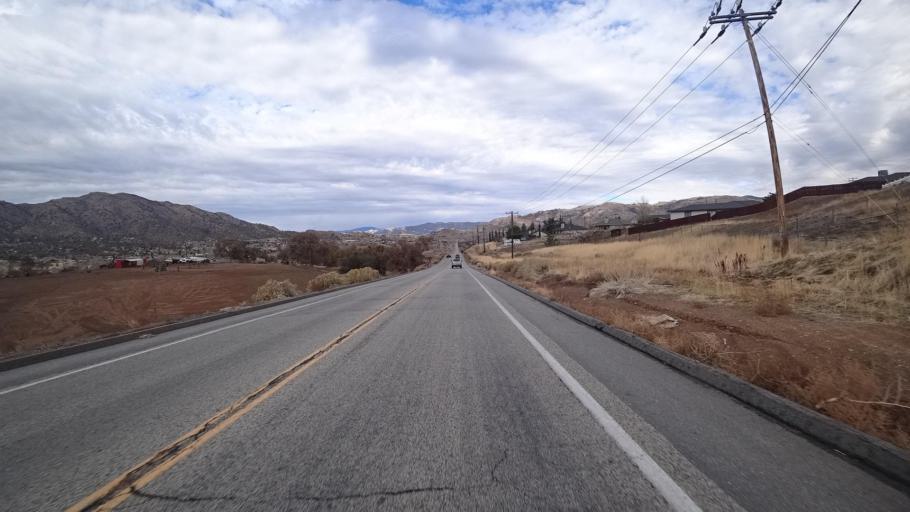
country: US
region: California
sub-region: Kern County
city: Golden Hills
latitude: 35.1376
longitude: -118.4948
